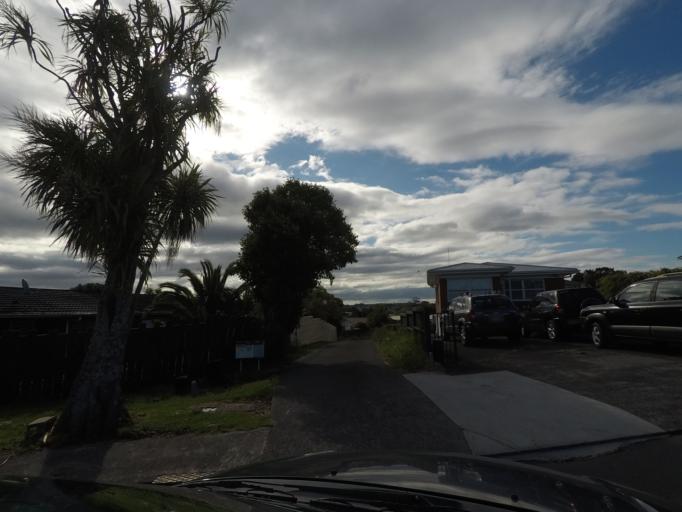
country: NZ
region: Auckland
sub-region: Auckland
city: Rosebank
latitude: -36.8716
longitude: 174.6413
